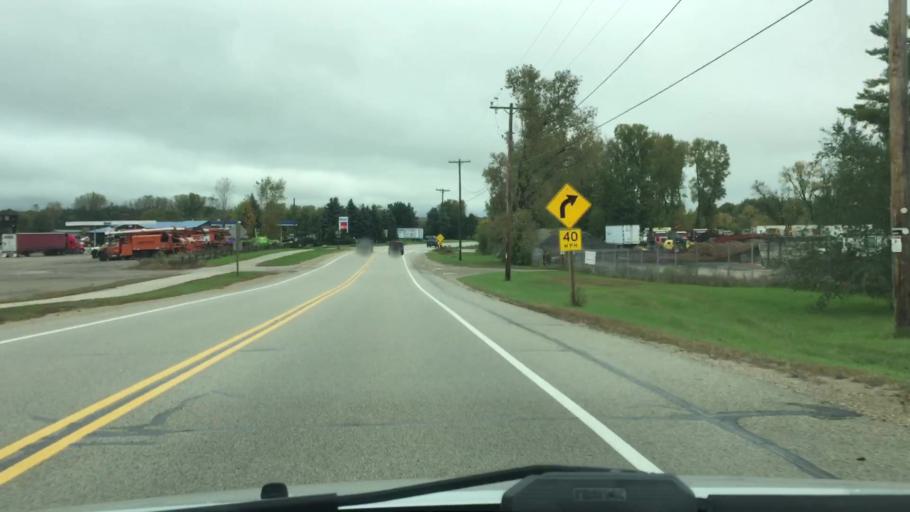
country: US
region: Wisconsin
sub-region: Waukesha County
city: Dousman
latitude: 43.0147
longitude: -88.4613
